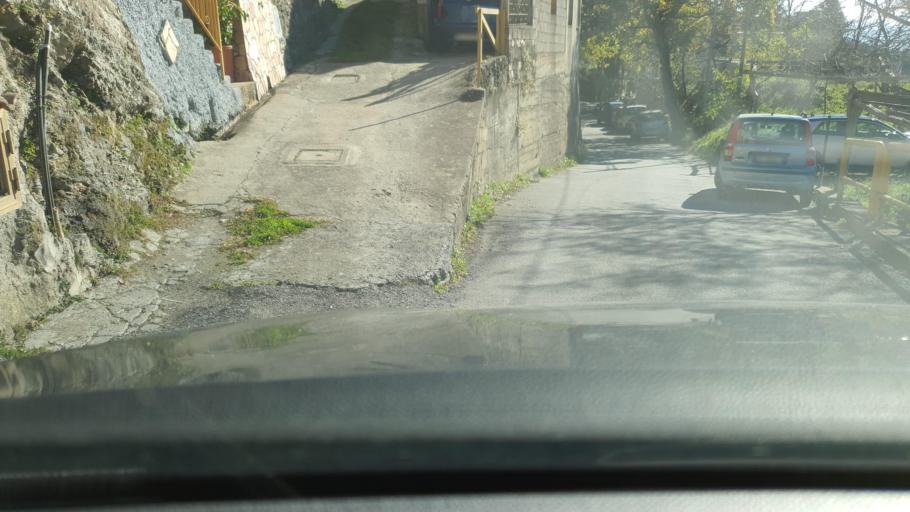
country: IT
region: Calabria
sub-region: Provincia di Catanzaro
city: Sant'Elia
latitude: 38.9563
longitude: 16.5812
